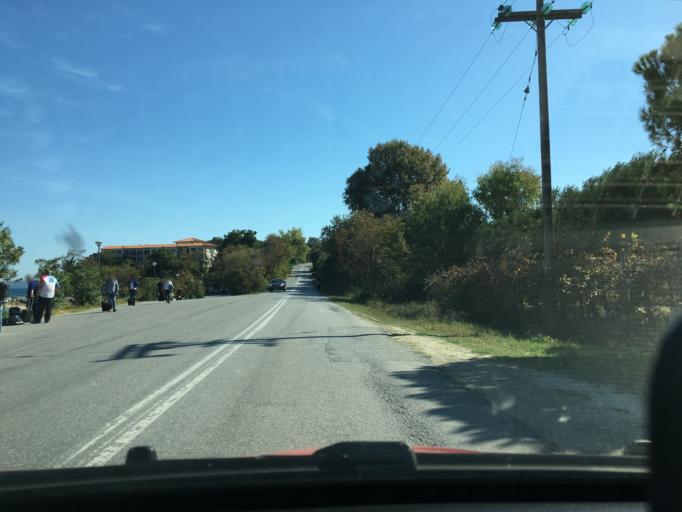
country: GR
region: Central Macedonia
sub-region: Nomos Chalkidikis
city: Ierissos
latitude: 40.3938
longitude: 23.8909
